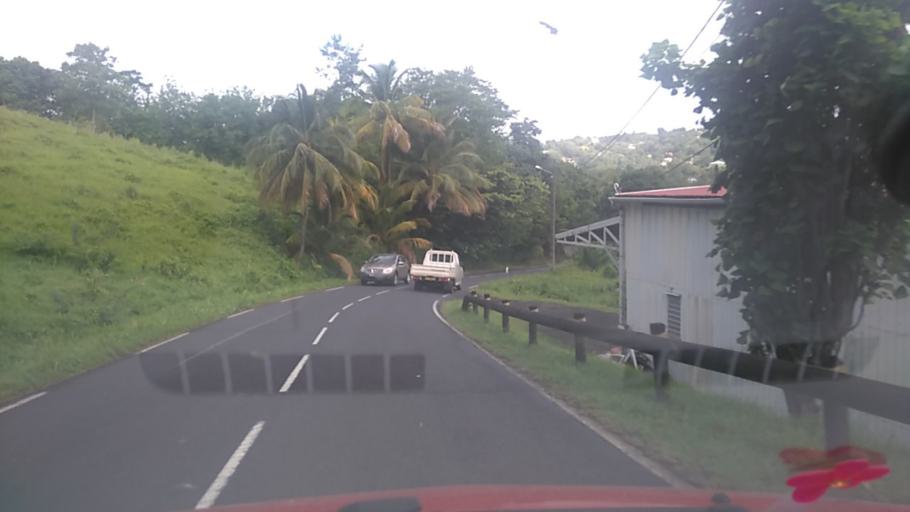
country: MQ
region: Martinique
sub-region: Martinique
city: Le Francois
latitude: 14.5984
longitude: -60.9300
